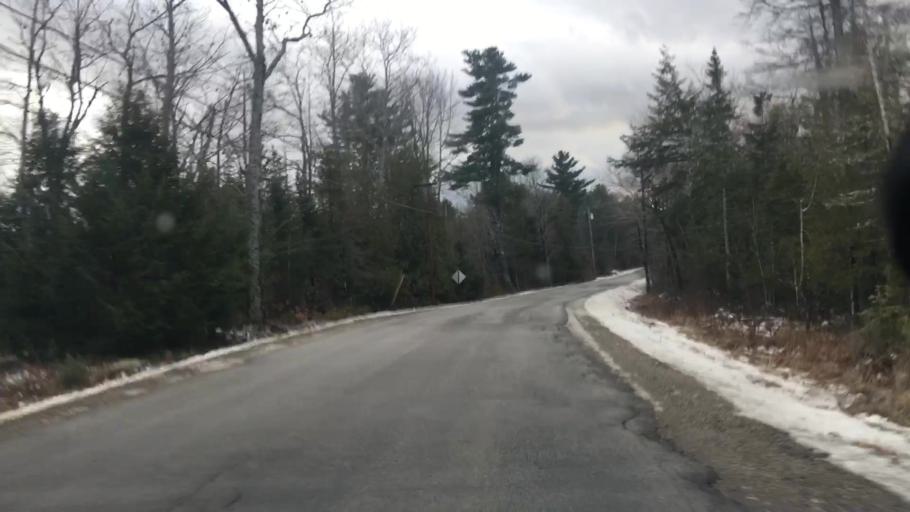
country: US
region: Maine
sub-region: Hancock County
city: Dedham
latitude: 44.6502
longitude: -68.7038
